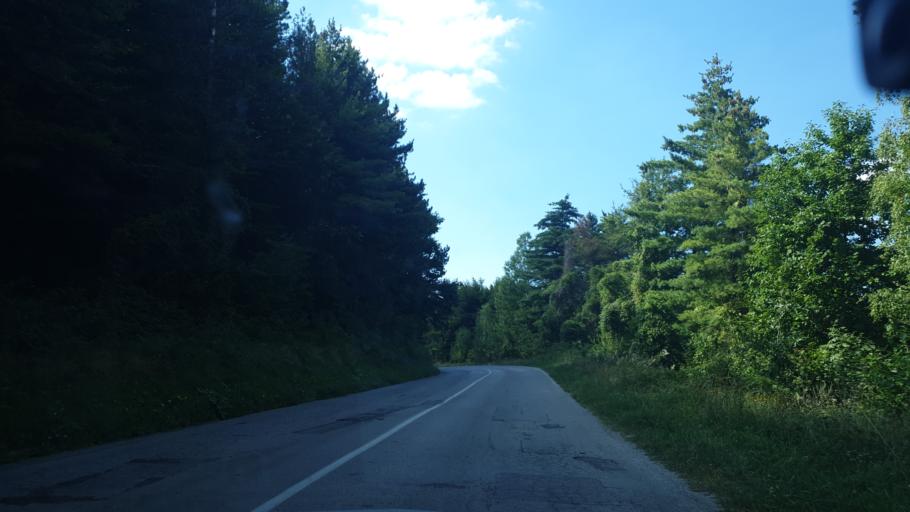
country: RS
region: Central Serbia
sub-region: Zlatiborski Okrug
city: Kosjeric
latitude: 44.0039
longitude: 20.0490
